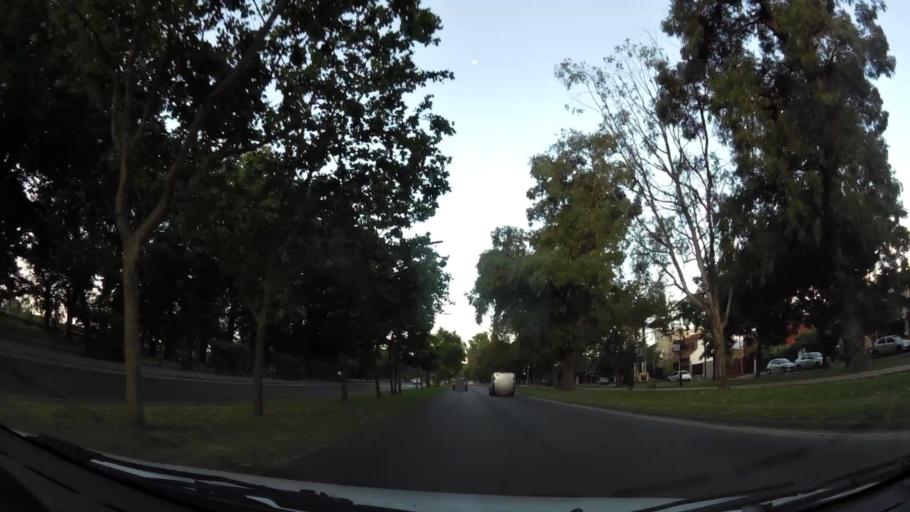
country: AR
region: Buenos Aires
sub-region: Partido de San Isidro
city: San Isidro
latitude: -34.4854
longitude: -58.5168
